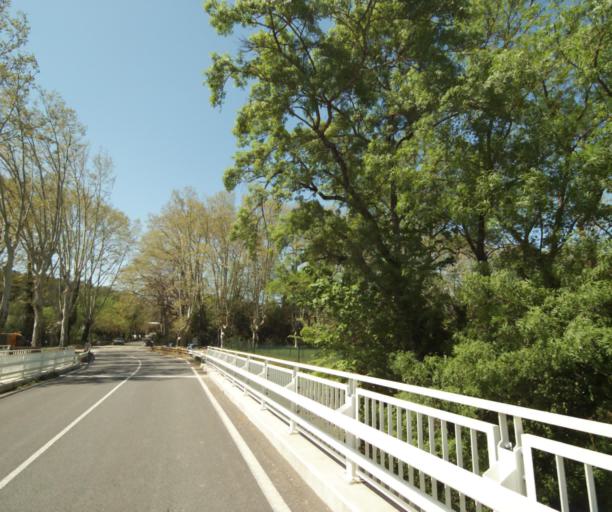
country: FR
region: Languedoc-Roussillon
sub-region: Departement de l'Herault
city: Prades-le-Lez
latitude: 43.7016
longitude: 3.8572
